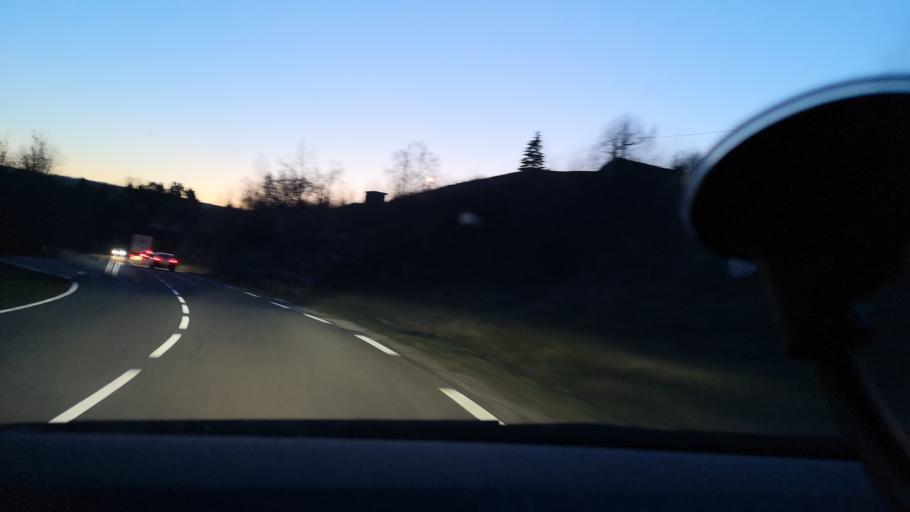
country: FR
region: Franche-Comte
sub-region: Departement du Jura
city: Champagnole
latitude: 46.7567
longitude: 5.9346
